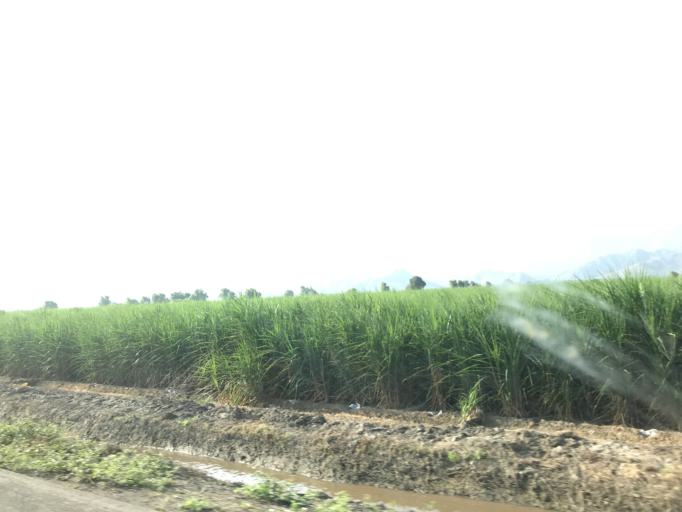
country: PE
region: Lambayeque
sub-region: Provincia de Chiclayo
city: Chongoyape
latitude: -6.6763
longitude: -79.4426
